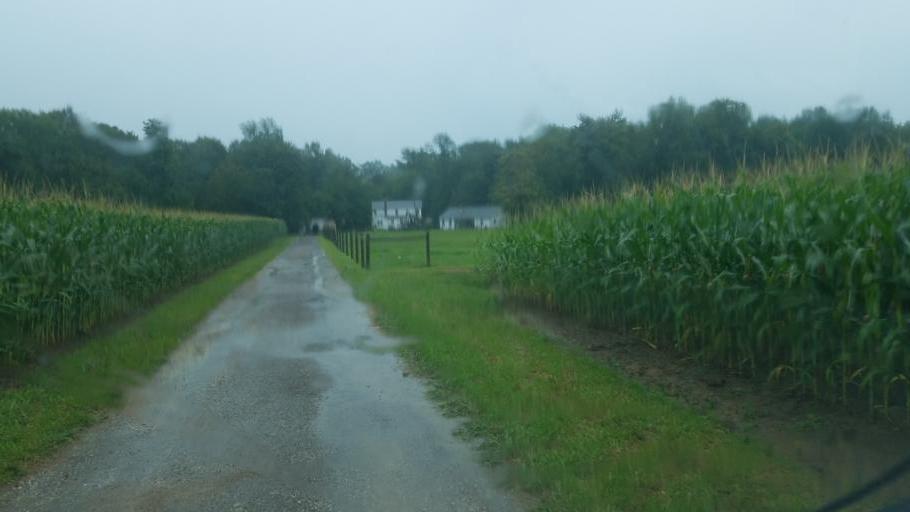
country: US
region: Ohio
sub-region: Geauga County
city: Middlefield
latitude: 41.4738
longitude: -80.9687
